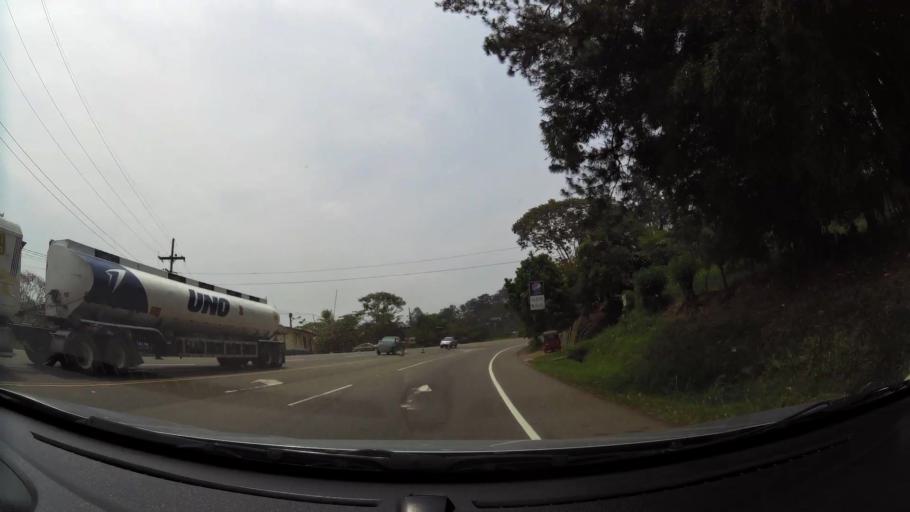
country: HN
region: Cortes
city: Agua Azul Rancho
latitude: 14.8929
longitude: -87.9428
